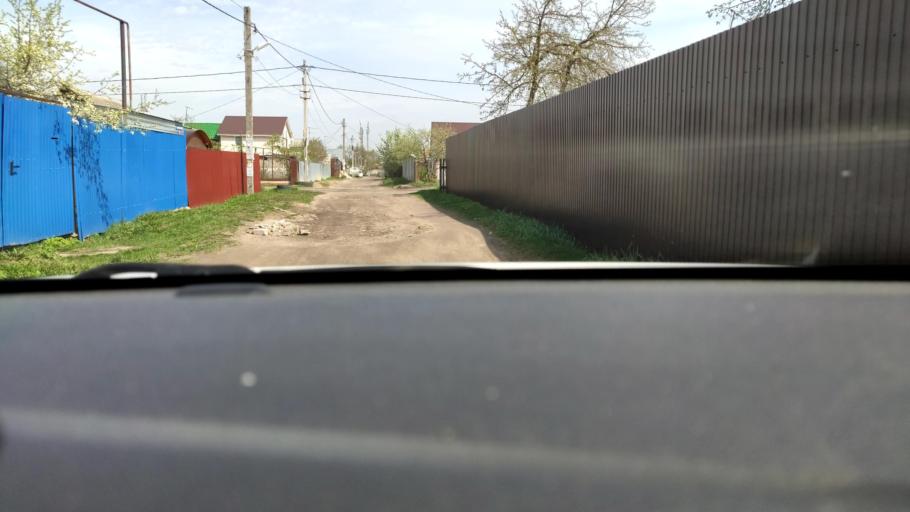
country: RU
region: Tatarstan
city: Osinovo
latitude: 55.8489
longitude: 48.8846
